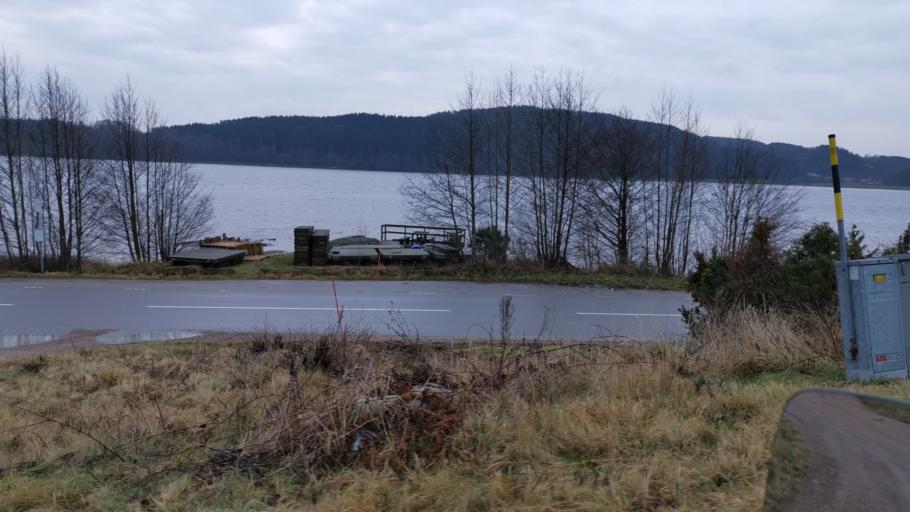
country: SE
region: Vaestra Goetaland
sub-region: Orust
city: Henan
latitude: 58.3383
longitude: 11.7148
